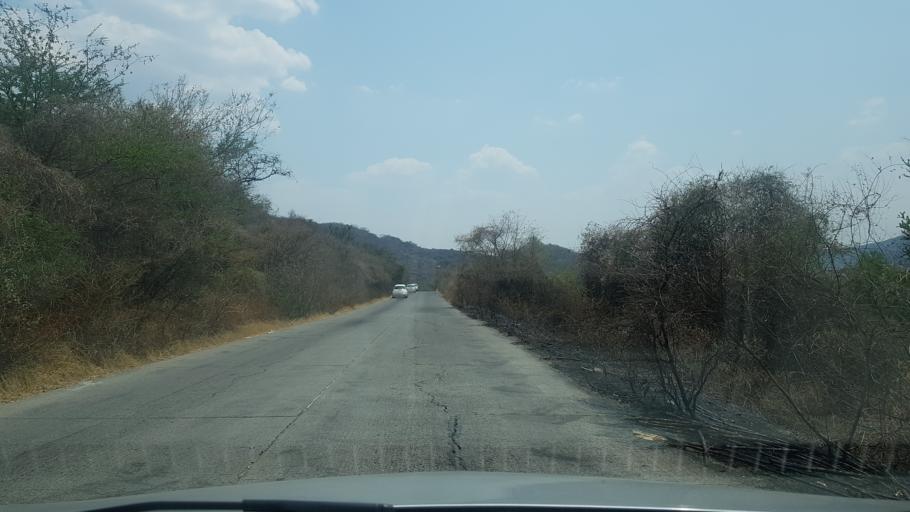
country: MX
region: Morelos
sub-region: Tlaltizapan de Zapata
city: Colonia Palo Prieto (Chipitongo)
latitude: 18.7643
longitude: -99.1077
